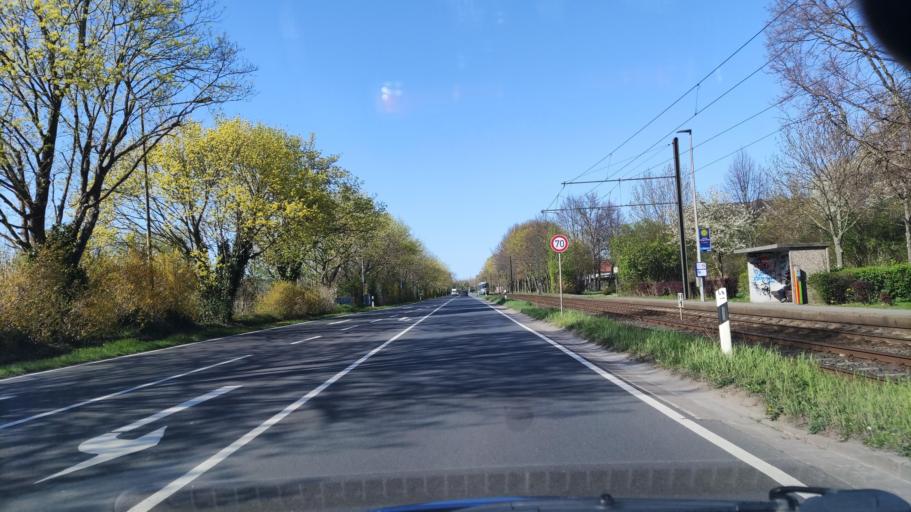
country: DE
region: Lower Saxony
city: Sarstedt
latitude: 52.2438
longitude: 9.8566
